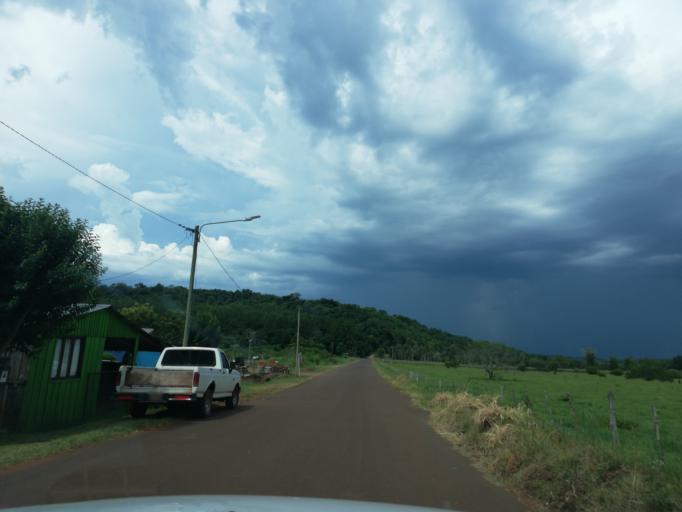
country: AR
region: Misiones
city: Cerro Azul
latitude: -27.5721
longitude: -55.4996
